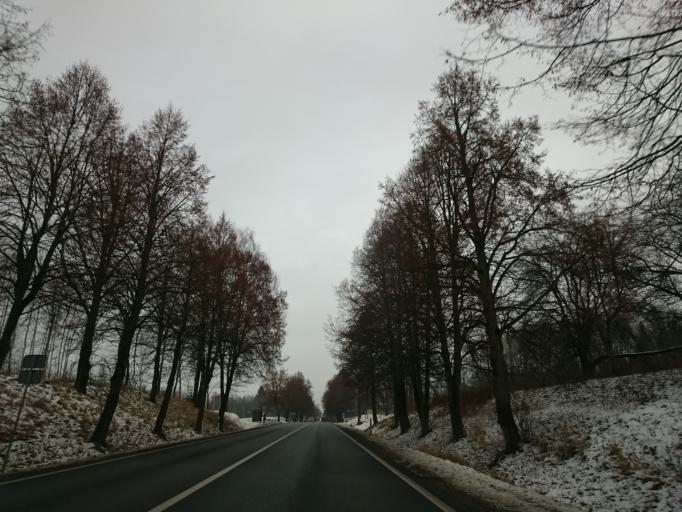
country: LV
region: Krimulda
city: Ragana
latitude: 57.1594
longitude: 24.6918
